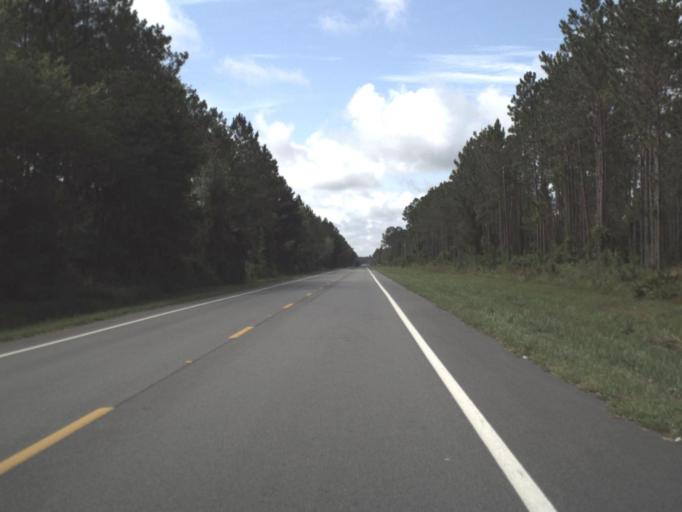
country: US
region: Florida
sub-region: Columbia County
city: Five Points
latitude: 30.3850
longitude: -82.6267
